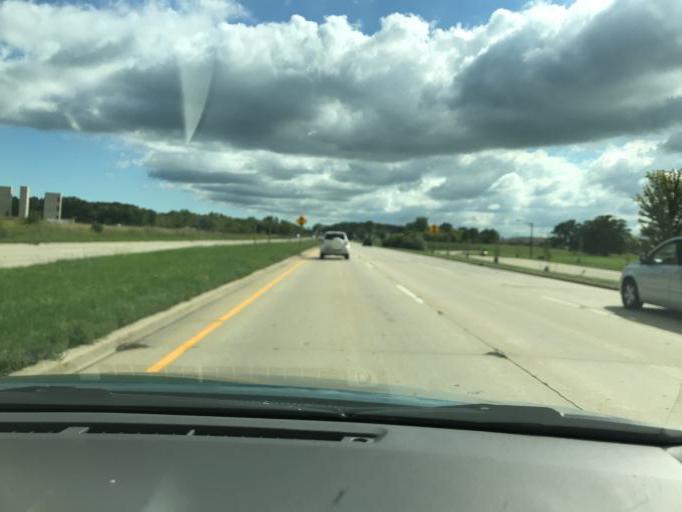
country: US
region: Wisconsin
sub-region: Kenosha County
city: Pleasant Prairie
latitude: 42.5267
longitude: -87.8921
